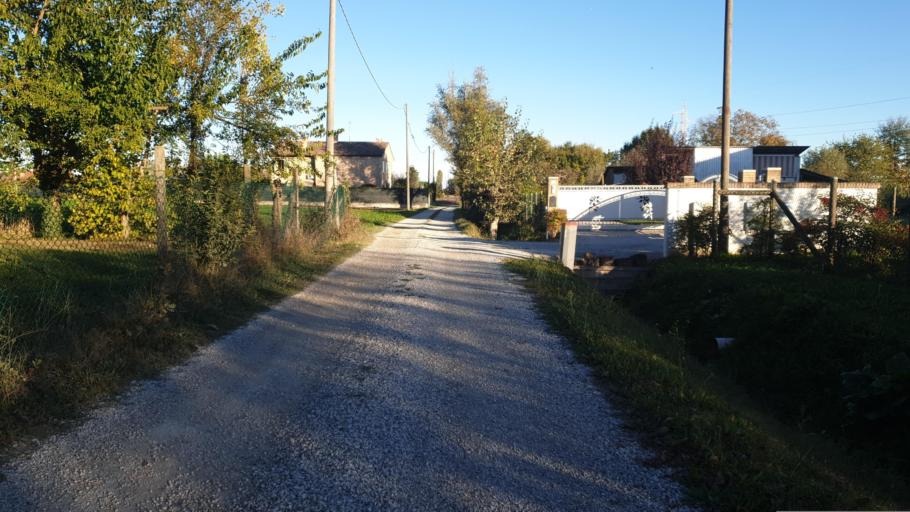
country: IT
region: Veneto
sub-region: Provincia di Venezia
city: Scaltenigo
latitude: 45.4678
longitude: 12.0976
